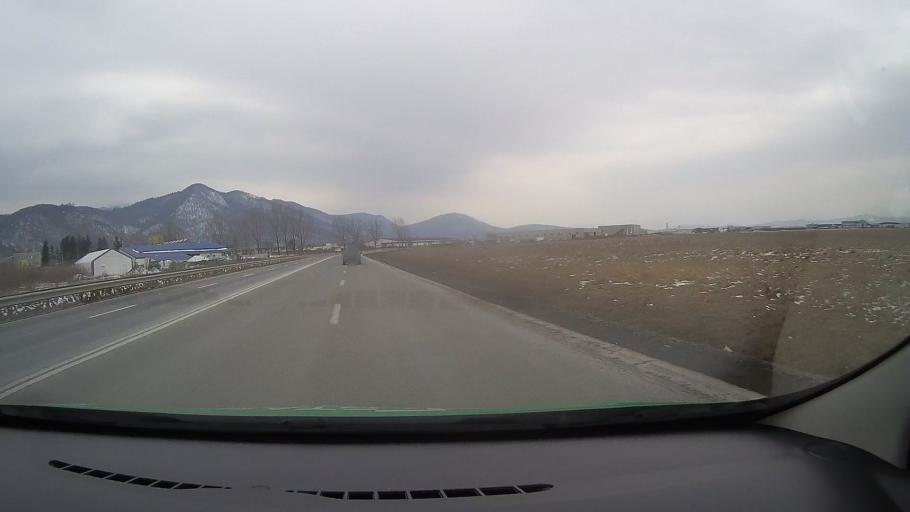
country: RO
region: Brasov
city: Brasov
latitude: 45.6579
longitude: 25.5558
